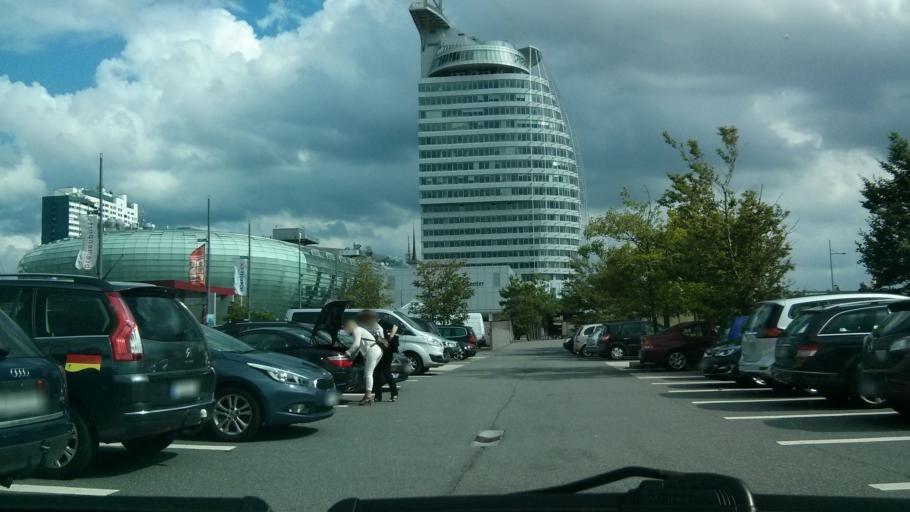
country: DE
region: Bremen
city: Bremerhaven
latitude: 53.5446
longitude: 8.5717
